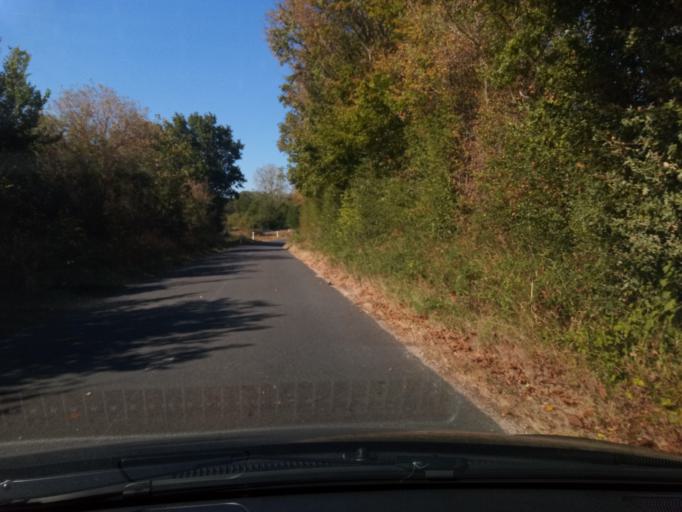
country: FR
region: Poitou-Charentes
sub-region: Departement de la Vienne
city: Montmorillon
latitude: 46.4783
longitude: 0.8965
